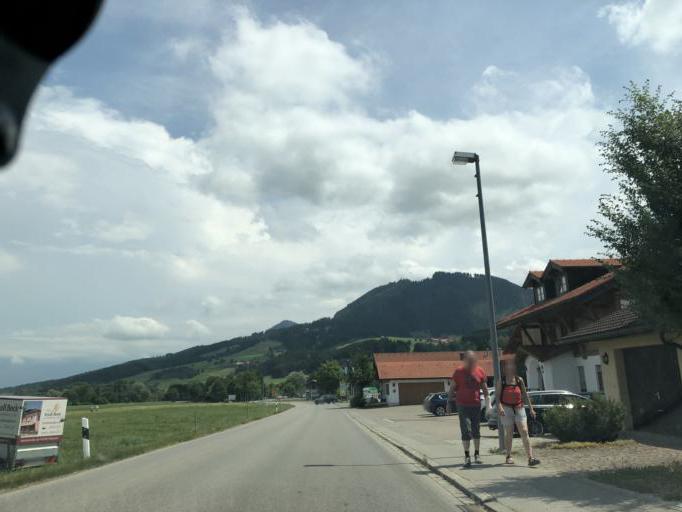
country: DE
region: Bavaria
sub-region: Swabia
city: Wertach
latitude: 47.6021
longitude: 10.4161
